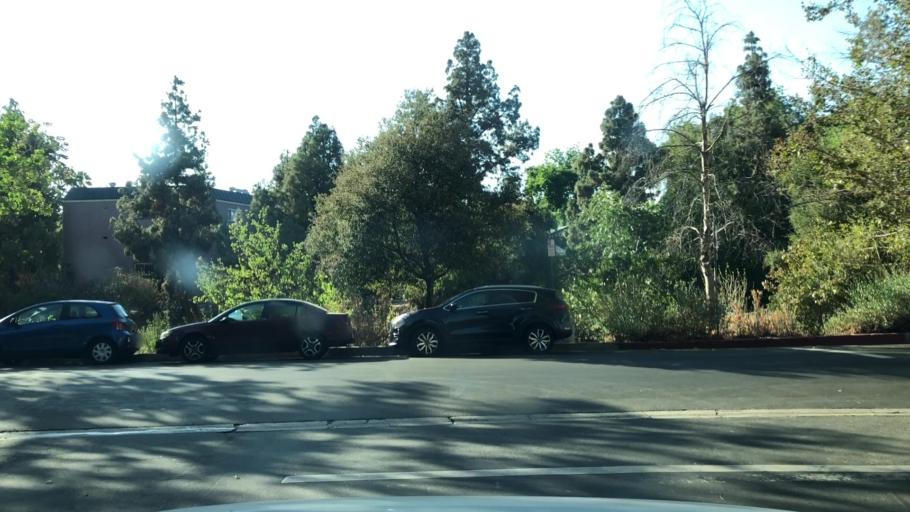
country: US
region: California
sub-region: Los Angeles County
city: North Hollywood
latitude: 34.1461
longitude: -118.3952
